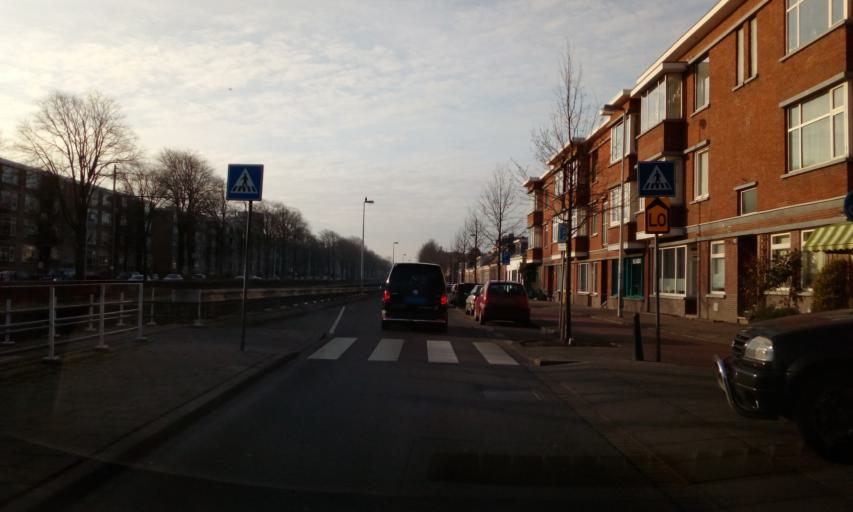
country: NL
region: South Holland
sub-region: Gemeente Den Haag
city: The Hague
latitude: 52.0657
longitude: 4.2665
